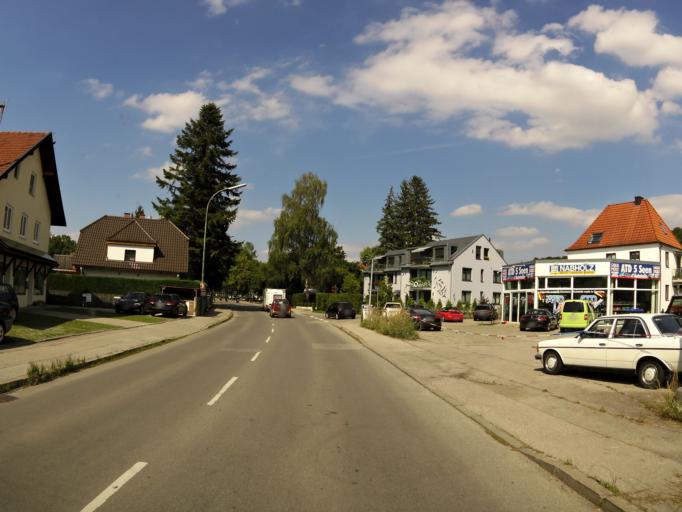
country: DE
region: Bavaria
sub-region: Upper Bavaria
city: Herrsching am Ammersee
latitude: 47.9918
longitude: 11.1729
